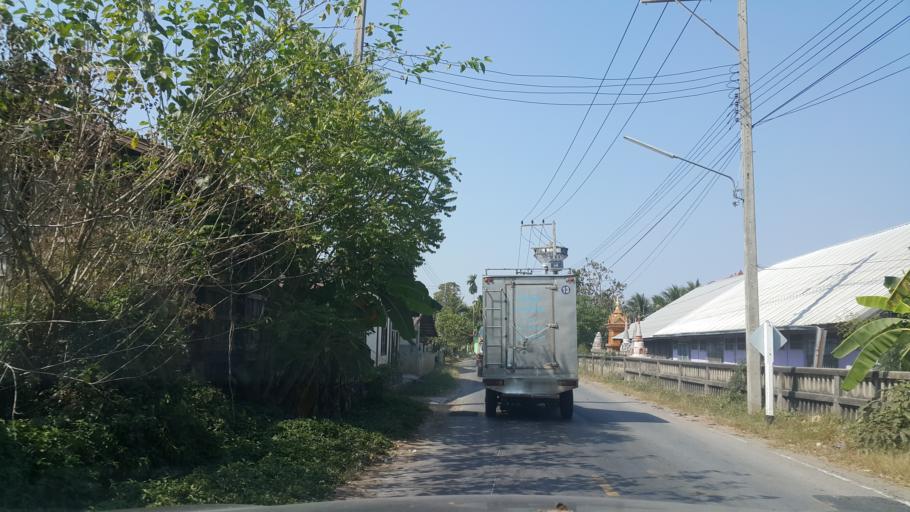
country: TH
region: Buriram
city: Krasang
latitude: 15.0534
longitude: 103.3852
